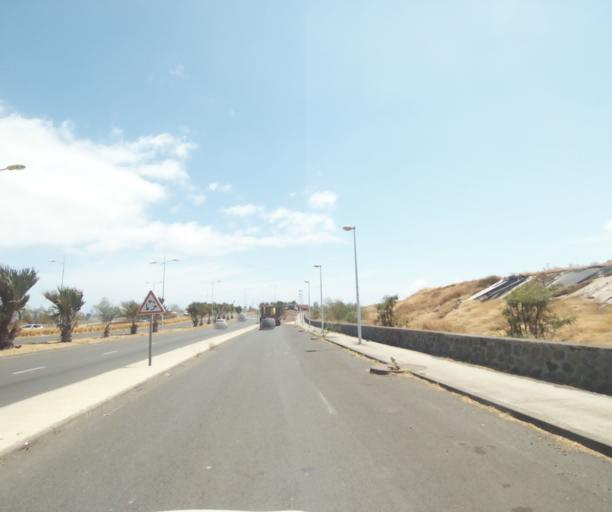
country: RE
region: Reunion
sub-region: Reunion
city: Le Port
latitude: -20.9610
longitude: 55.2939
